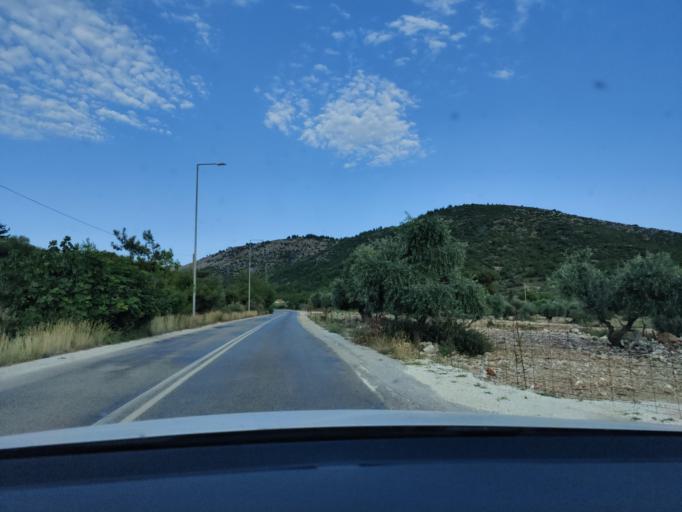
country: GR
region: East Macedonia and Thrace
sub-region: Nomos Kavalas
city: Limenaria
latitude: 40.6134
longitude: 24.6257
